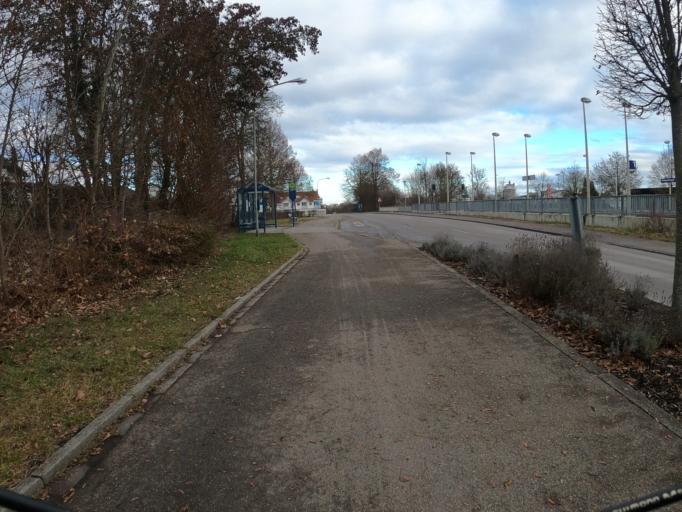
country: DE
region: Bavaria
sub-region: Swabia
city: Nersingen
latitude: 48.4533
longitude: 10.1002
